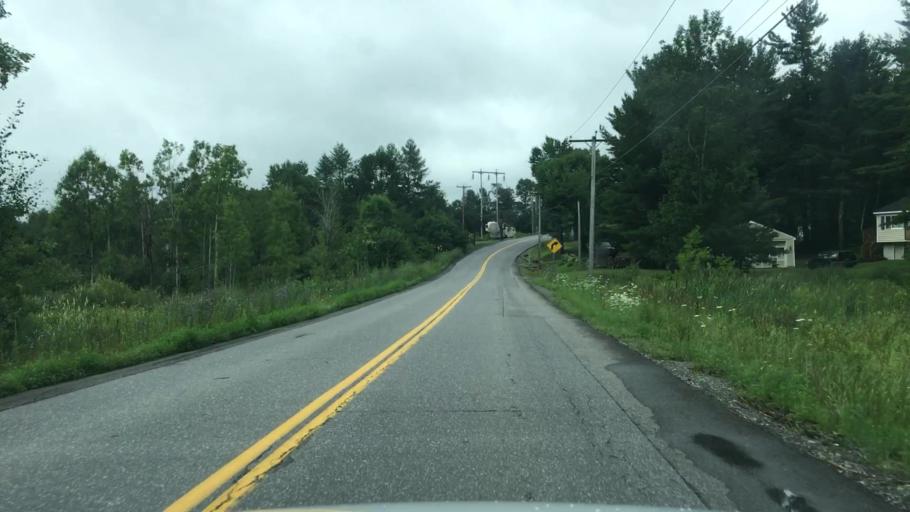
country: US
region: Maine
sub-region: Kennebec County
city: Augusta
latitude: 44.3225
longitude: -69.7337
